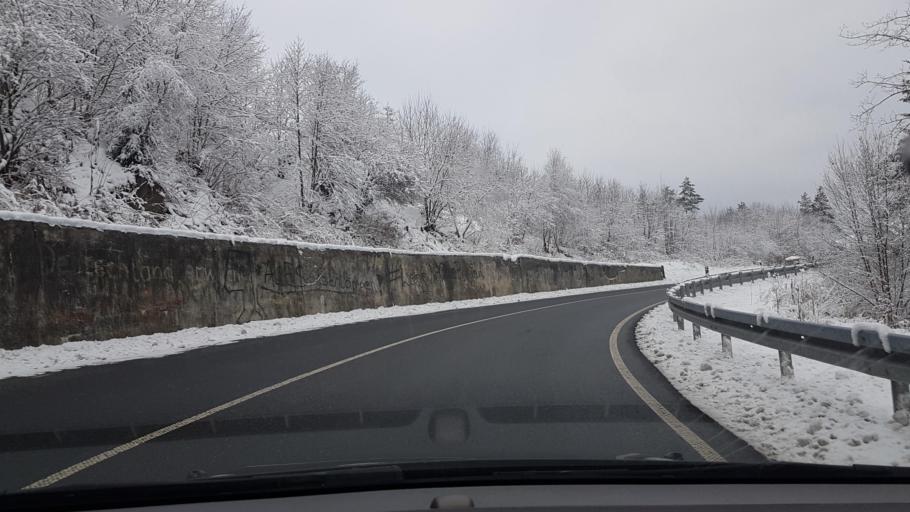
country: DE
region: Lower Saxony
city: Clausthal-Zellerfeld
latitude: 51.8044
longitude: 10.3079
